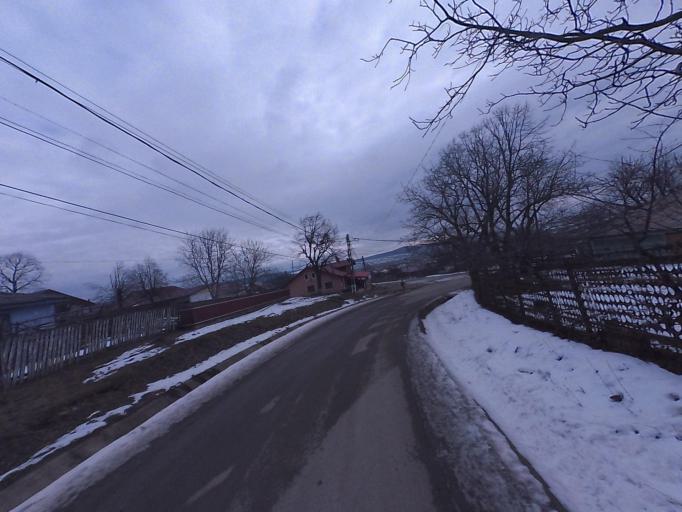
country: RO
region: Iasi
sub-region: Comuna Tibanesti
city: Glodenii Gandului
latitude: 46.9787
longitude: 27.3036
